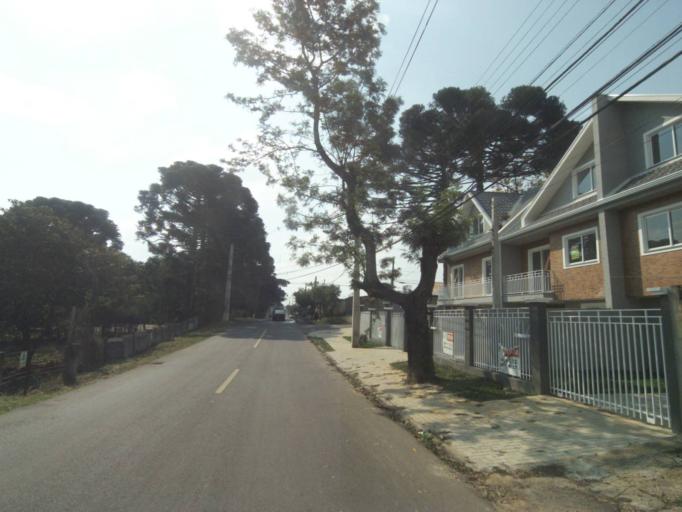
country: BR
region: Parana
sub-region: Sao Jose Dos Pinhais
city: Sao Jose dos Pinhais
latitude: -25.5148
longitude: -49.2485
